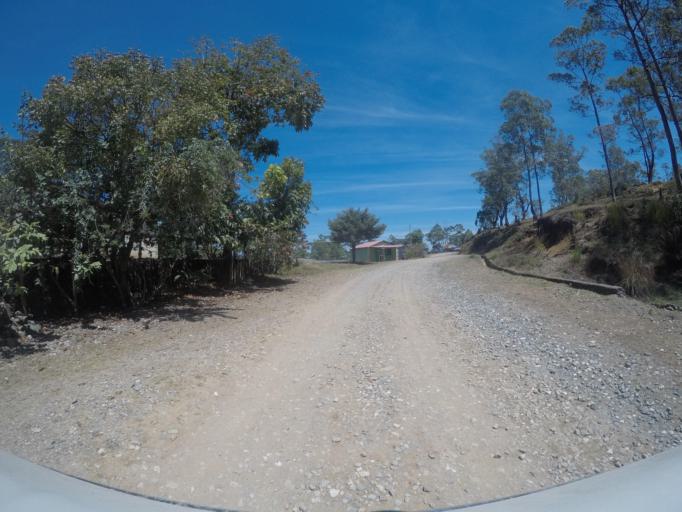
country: TL
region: Ermera
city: Gleno
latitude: -8.7859
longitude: 125.3754
